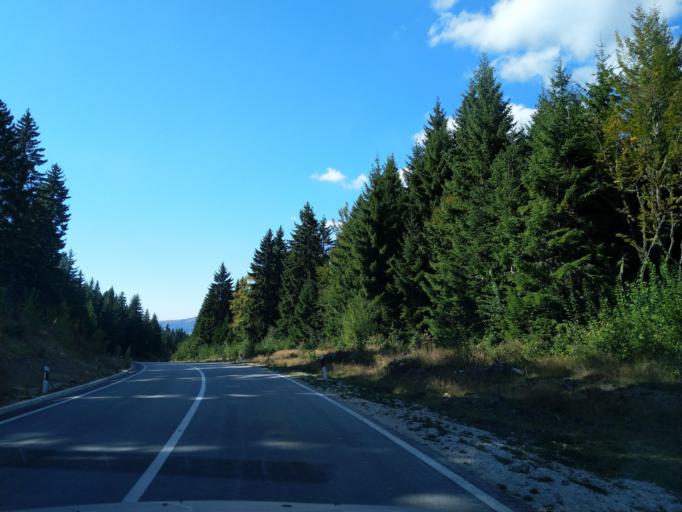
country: RS
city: Sokolovica
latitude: 43.2850
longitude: 20.3241
